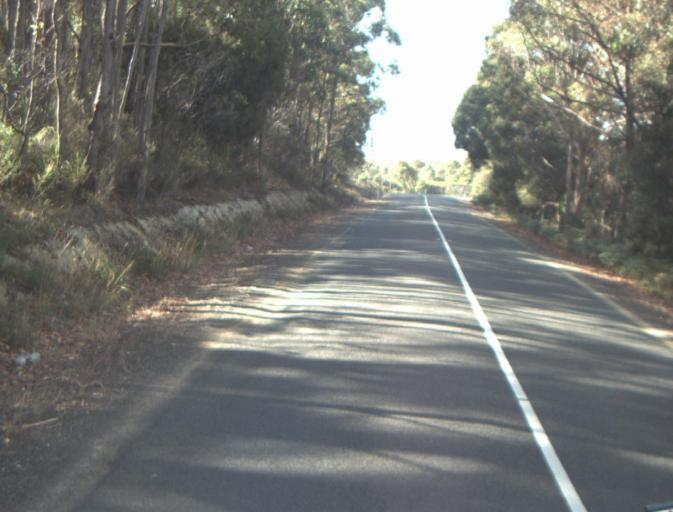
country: AU
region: Tasmania
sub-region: Dorset
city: Bridport
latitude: -41.1471
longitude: 147.2327
